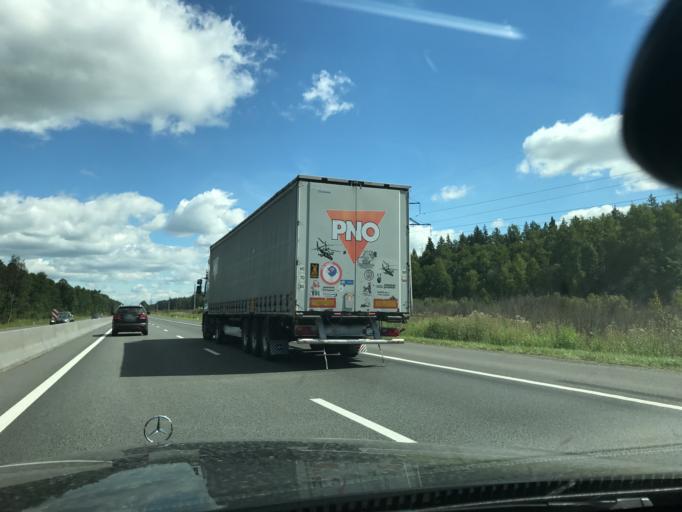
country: RU
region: Nizjnij Novgorod
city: Volodarsk
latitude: 56.2856
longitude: 43.1766
